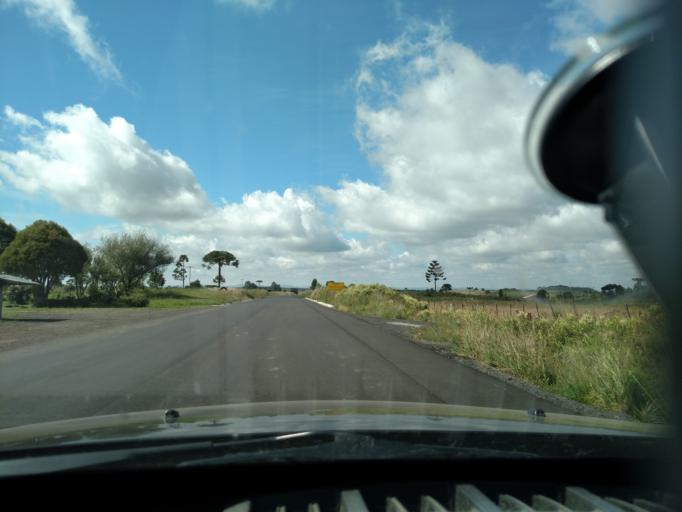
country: BR
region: Santa Catarina
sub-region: Lages
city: Lages
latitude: -27.9772
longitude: -50.0933
